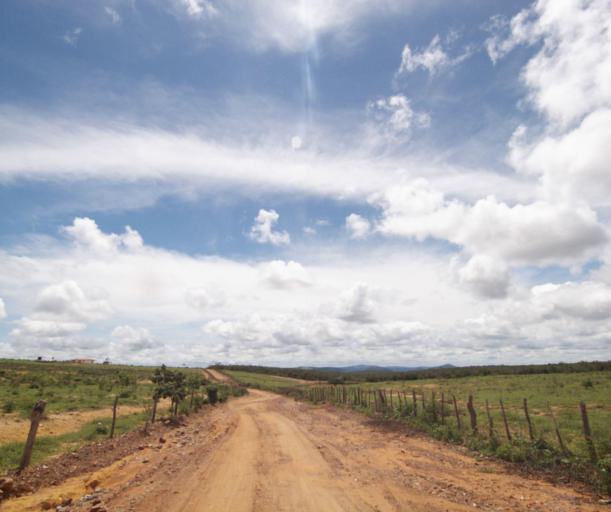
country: BR
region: Bahia
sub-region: Tanhacu
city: Tanhacu
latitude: -14.1928
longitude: -41.0580
